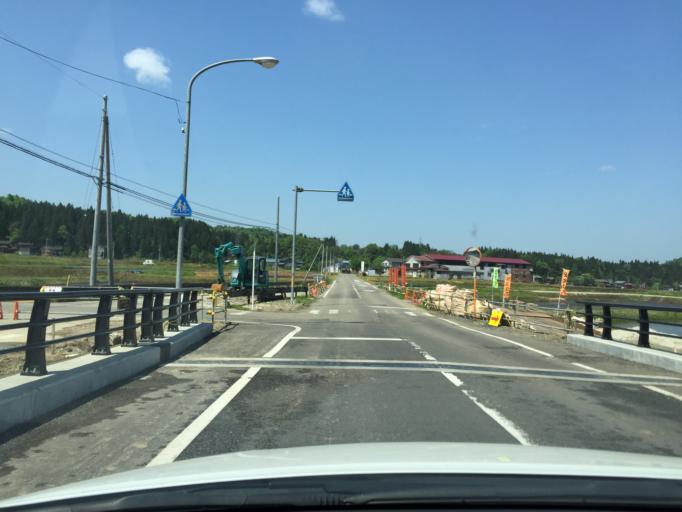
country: JP
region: Niigata
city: Tochio-honcho
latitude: 37.5049
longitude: 139.0612
